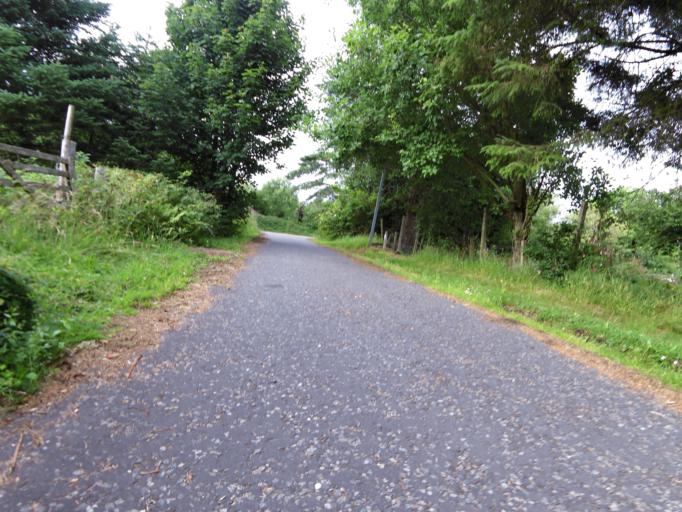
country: GB
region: Scotland
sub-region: Argyll and Bute
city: Isle Of Mull
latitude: 56.9113
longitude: -5.8423
